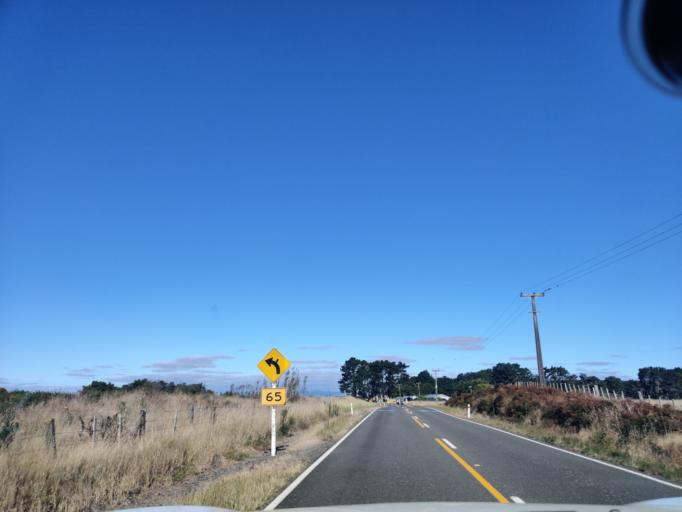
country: NZ
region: Manawatu-Wanganui
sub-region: Horowhenua District
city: Foxton
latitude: -40.3847
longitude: 175.2770
